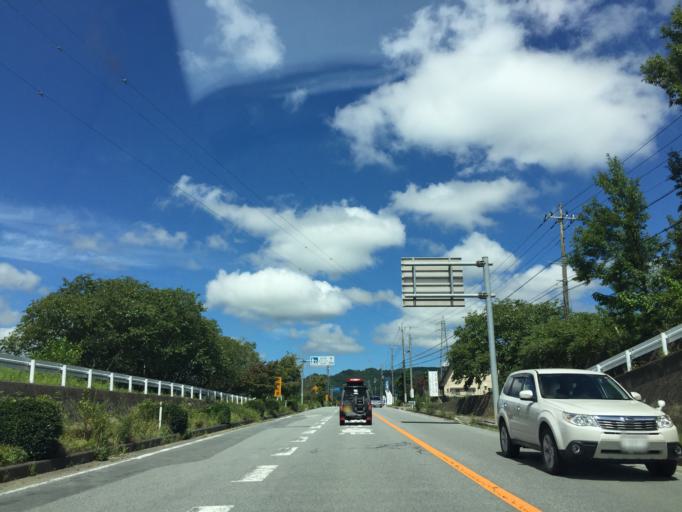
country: JP
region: Yamanashi
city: Nirasaki
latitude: 35.8039
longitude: 138.3542
